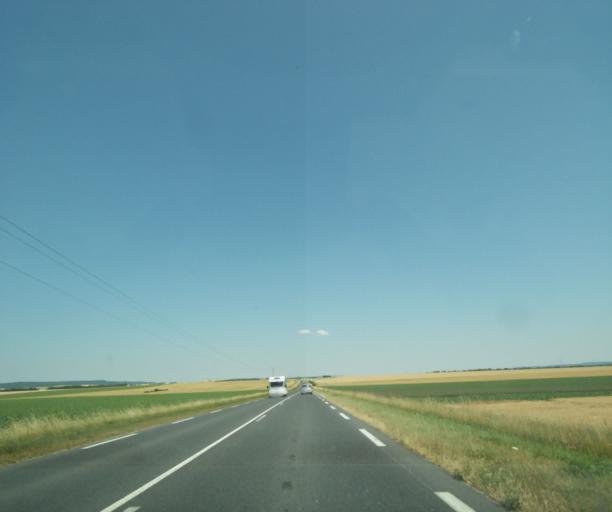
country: FR
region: Champagne-Ardenne
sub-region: Departement de la Marne
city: Mourmelon-le-Grand
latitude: 49.0910
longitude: 4.2736
